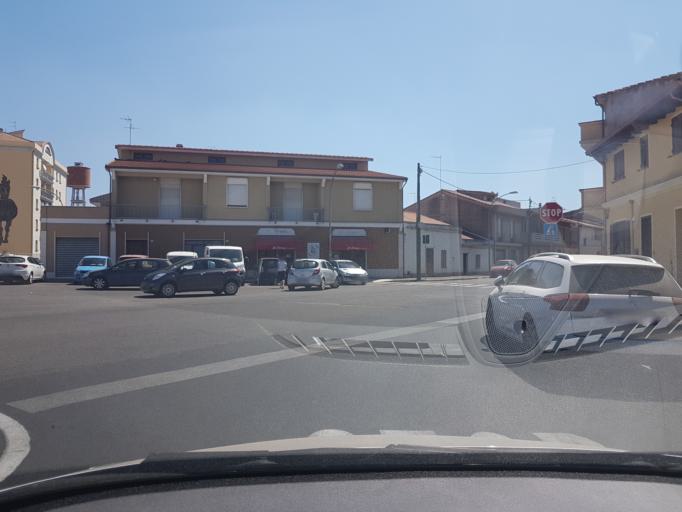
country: IT
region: Sardinia
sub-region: Provincia di Oristano
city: Oristano
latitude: 39.8999
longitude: 8.6015
